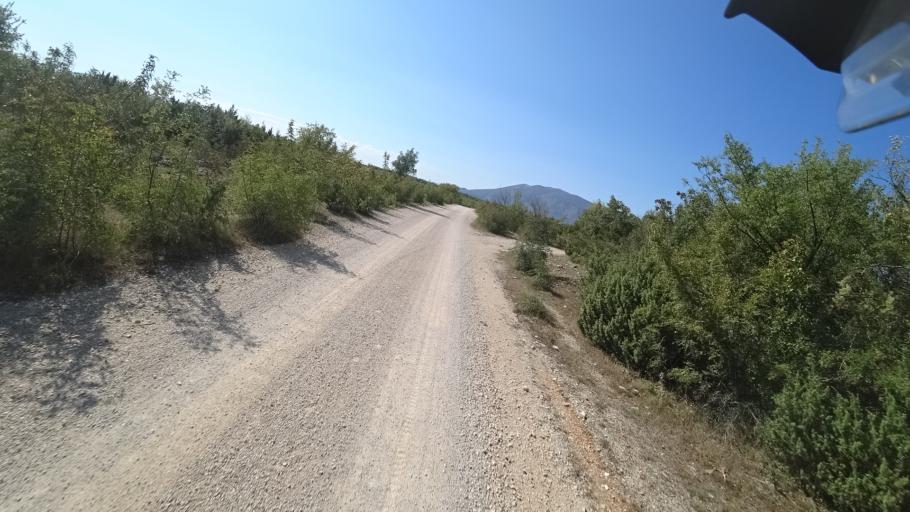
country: HR
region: Sibensko-Kniniska
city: Knin
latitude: 43.9956
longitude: 16.1933
